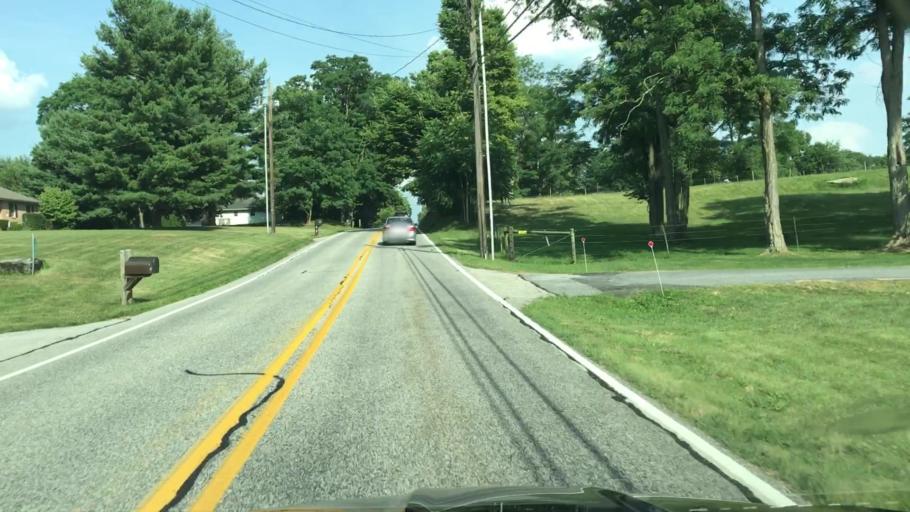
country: US
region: Pennsylvania
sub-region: Cumberland County
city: Boiling Springs
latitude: 40.1767
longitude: -77.0764
